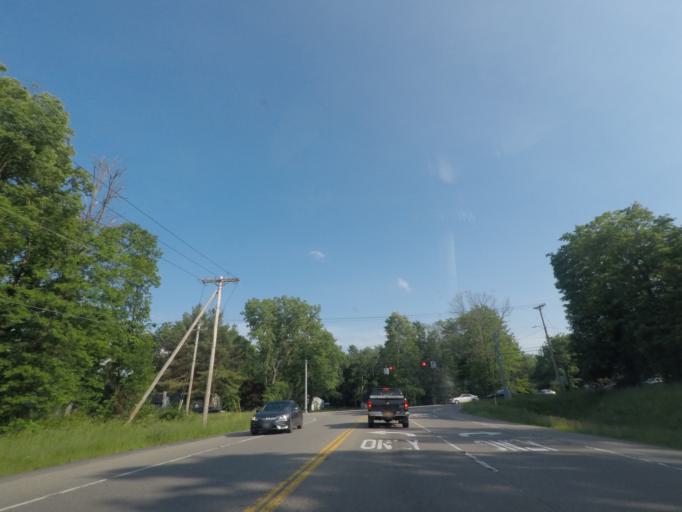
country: US
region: New York
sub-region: Orange County
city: Beaverdam Lake-Salisbury Mills
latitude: 41.4786
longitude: -74.1295
